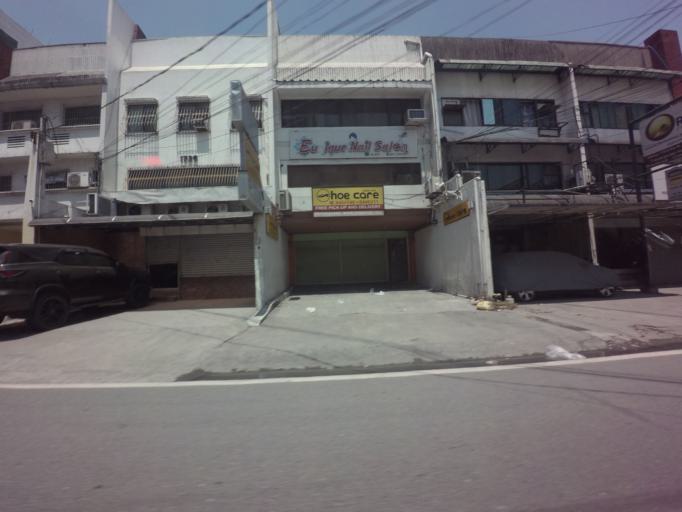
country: PH
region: Metro Manila
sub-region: Makati City
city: Makati City
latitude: 14.5576
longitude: 121.0035
